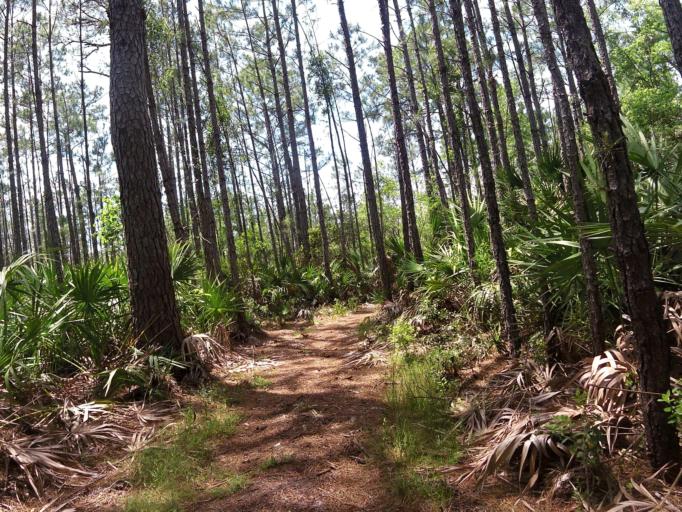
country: US
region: Florida
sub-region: Nassau County
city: Yulee
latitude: 30.4985
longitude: -81.4970
